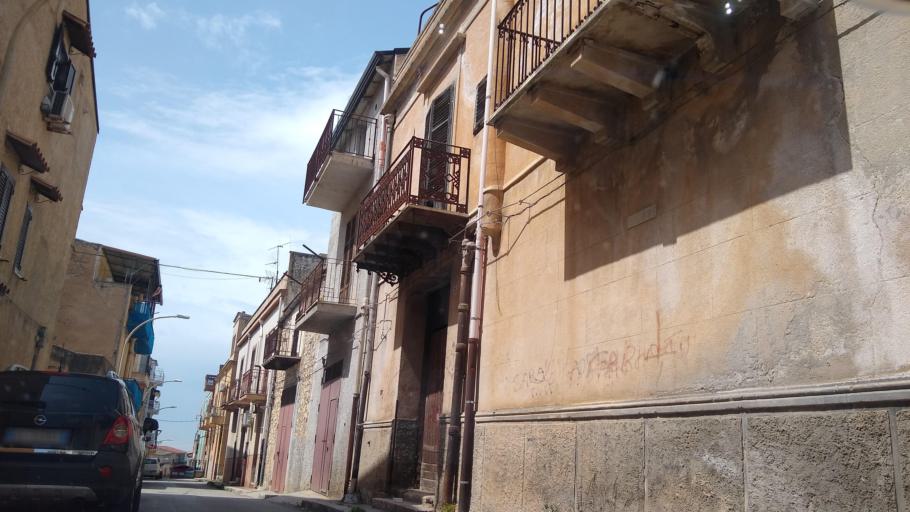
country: IT
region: Sicily
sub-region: Palermo
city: San Cipirello
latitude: 37.9629
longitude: 13.1751
